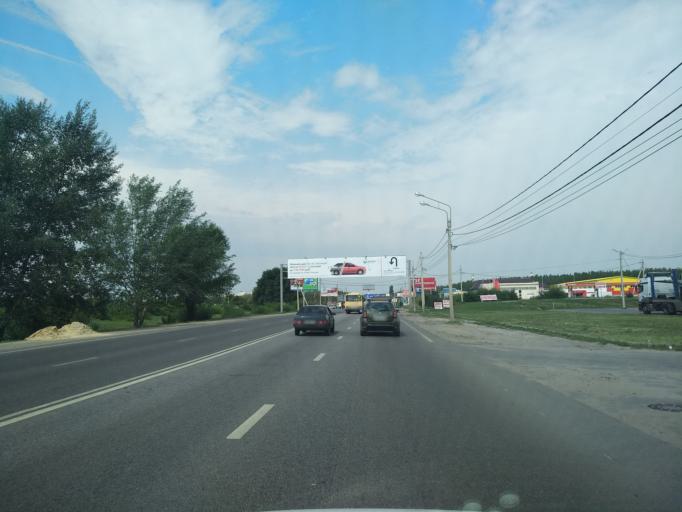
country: RU
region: Voronezj
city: Somovo
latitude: 51.6796
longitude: 39.2886
